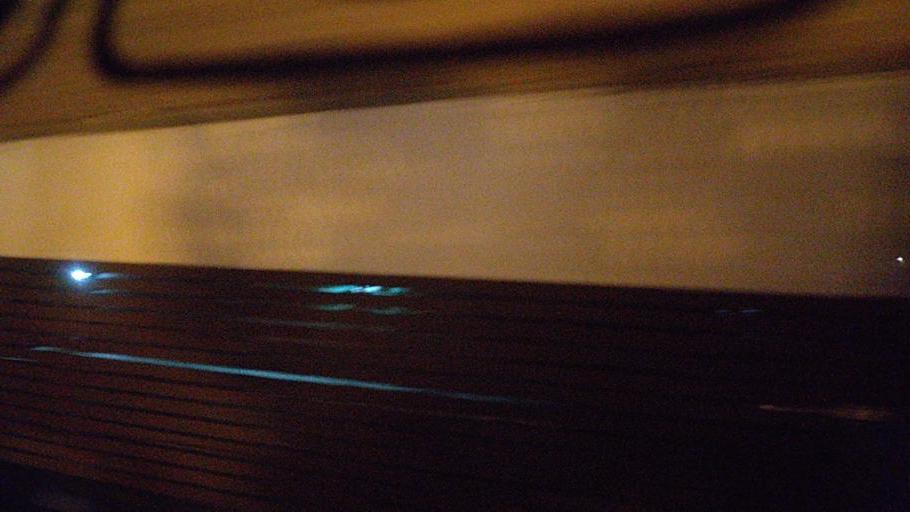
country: TH
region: Bangkok
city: Sai Mai
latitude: 13.9329
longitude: 100.6857
